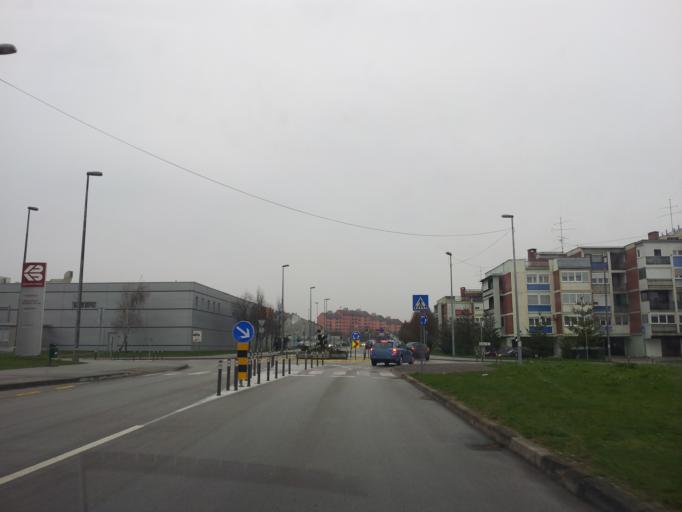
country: HR
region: Karlovacka
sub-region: Grad Karlovac
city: Karlovac
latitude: 45.4826
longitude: 15.5495
